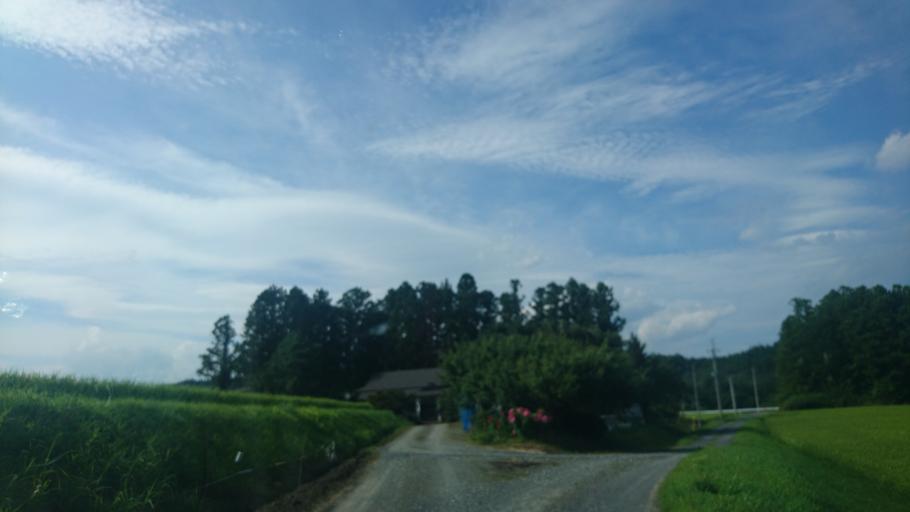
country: JP
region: Miyagi
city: Furukawa
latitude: 38.7654
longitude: 140.9532
